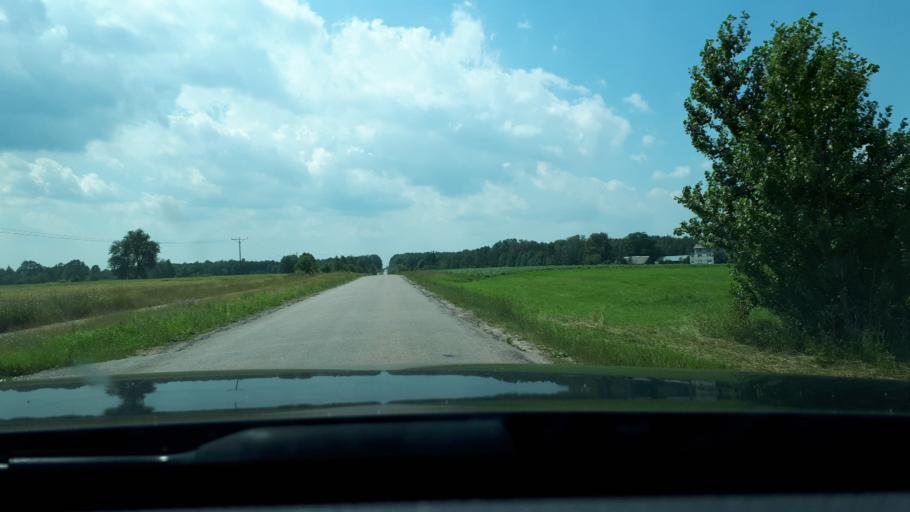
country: PL
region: Podlasie
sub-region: Powiat bialostocki
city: Choroszcz
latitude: 53.1233
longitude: 22.9361
